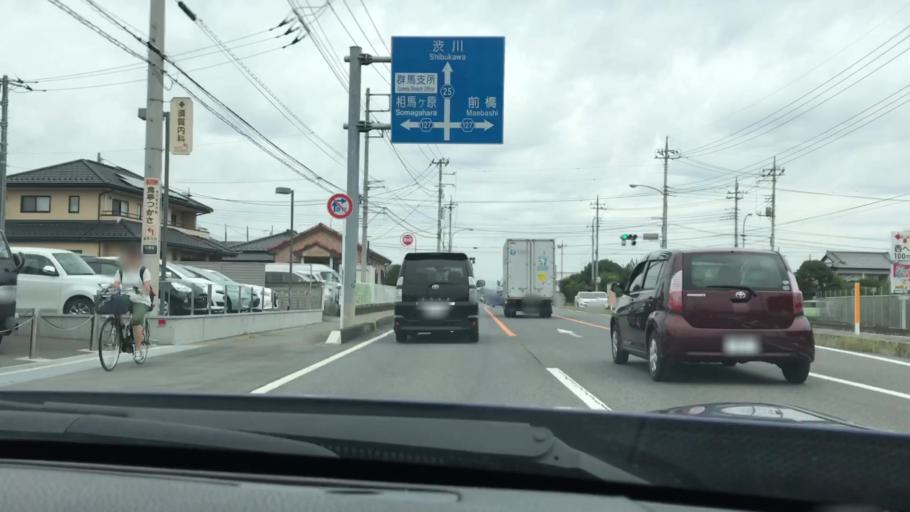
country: JP
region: Gunma
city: Kanekomachi
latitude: 36.3942
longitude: 139.0078
